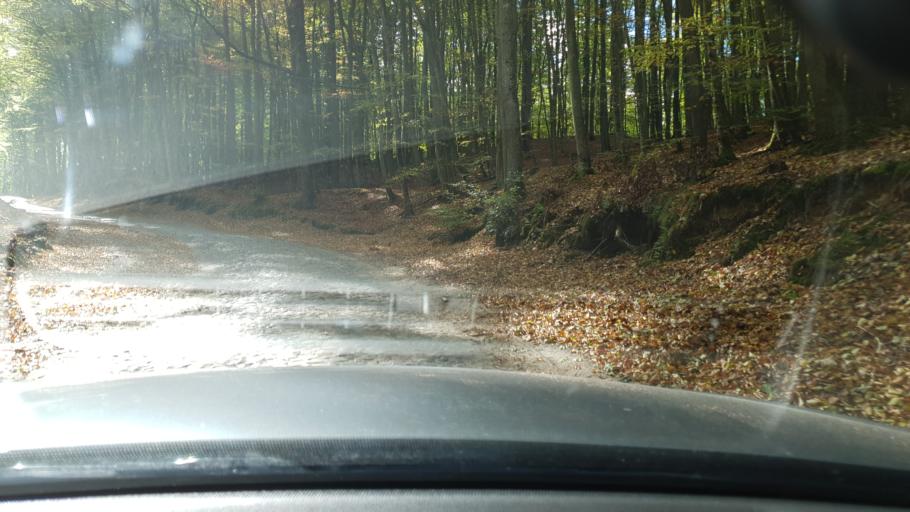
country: PL
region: Pomeranian Voivodeship
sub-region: Powiat wejherowski
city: Reda
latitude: 54.5853
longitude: 18.3171
